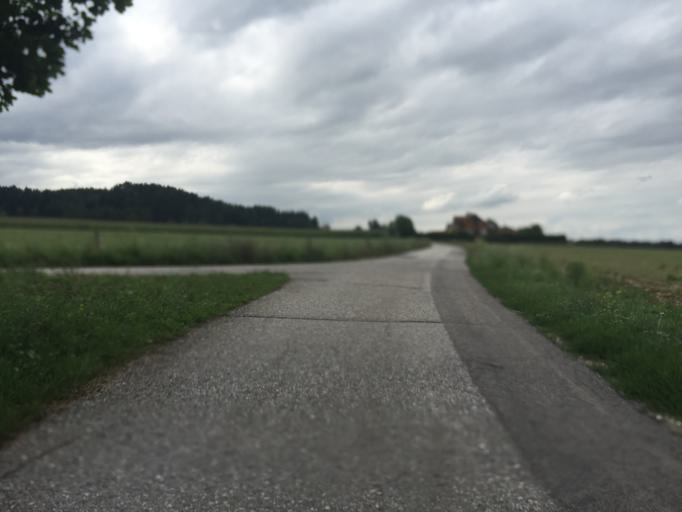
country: AT
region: Carinthia
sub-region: Politischer Bezirk Volkermarkt
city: Feistritz ob Bleiburg
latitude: 46.5555
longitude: 14.7840
